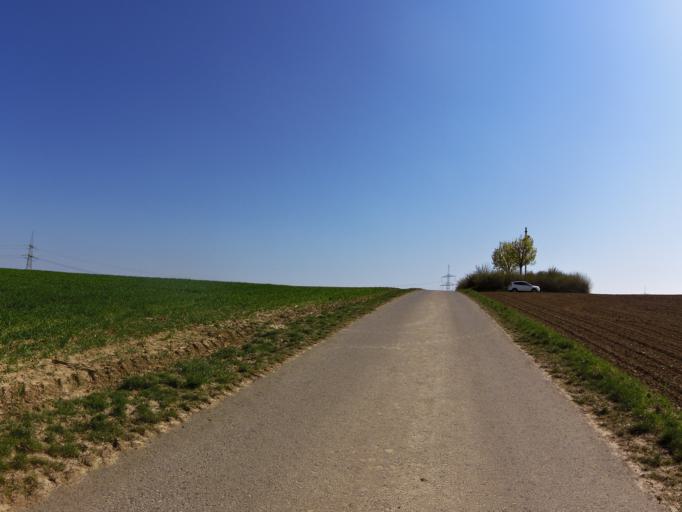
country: DE
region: Bavaria
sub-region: Regierungsbezirk Unterfranken
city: Rottendorf
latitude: 49.8168
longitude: 10.0757
